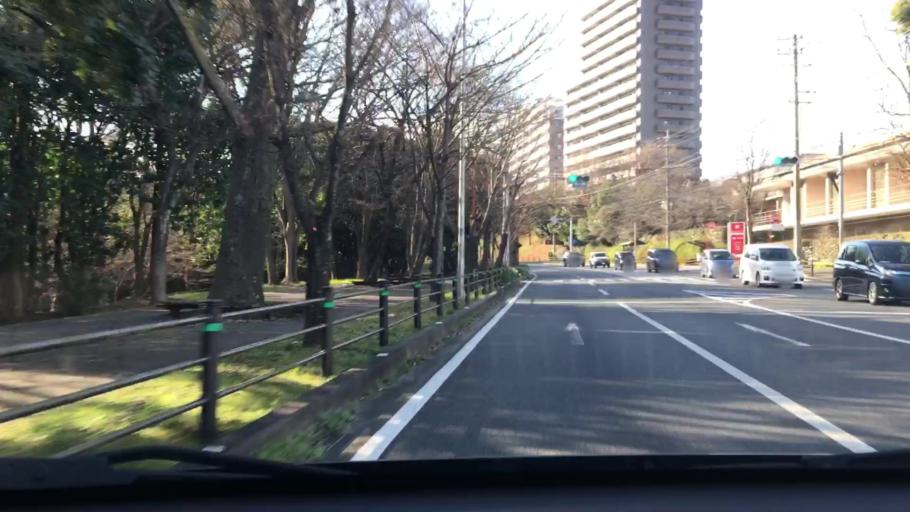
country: JP
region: Oita
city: Tsurusaki
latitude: 33.2255
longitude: 131.6564
